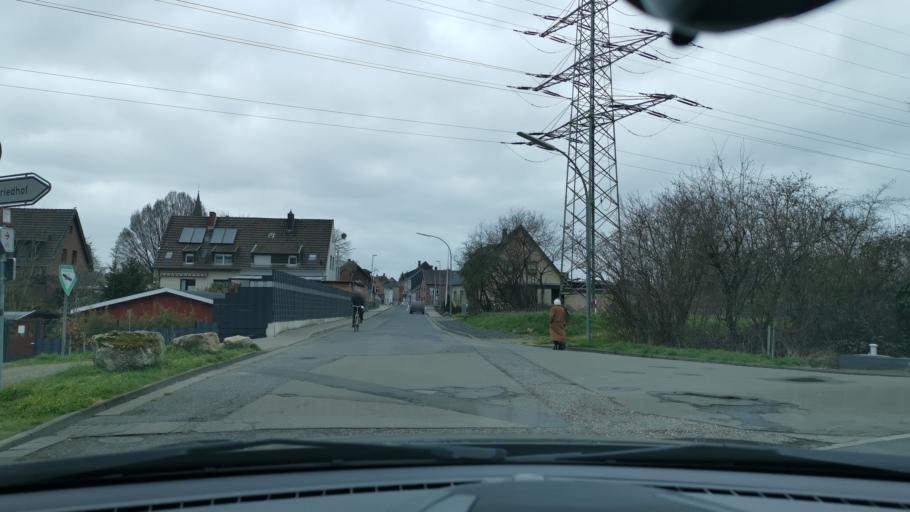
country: DE
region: North Rhine-Westphalia
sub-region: Regierungsbezirk Dusseldorf
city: Grevenbroich
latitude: 51.0707
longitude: 6.5724
